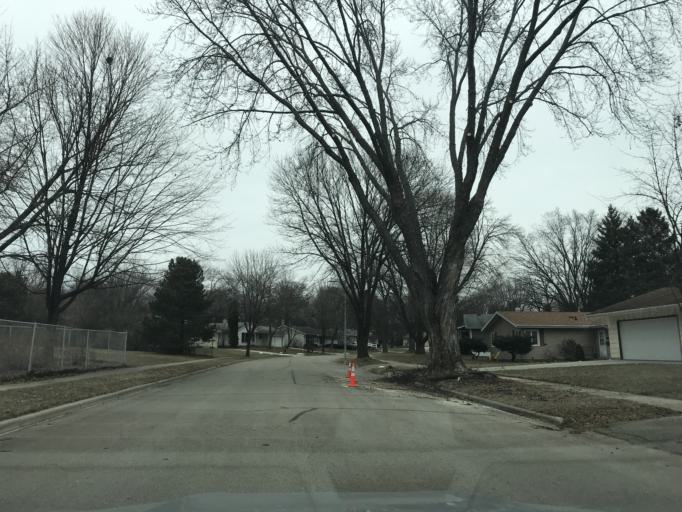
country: US
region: Wisconsin
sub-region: Dane County
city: Monona
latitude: 43.0903
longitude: -89.3052
